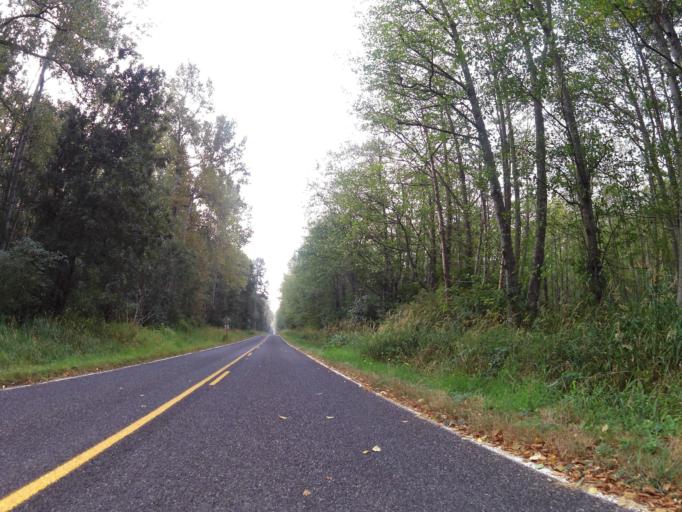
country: US
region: Washington
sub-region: Whatcom County
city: Birch Bay
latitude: 48.8700
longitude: -122.7318
